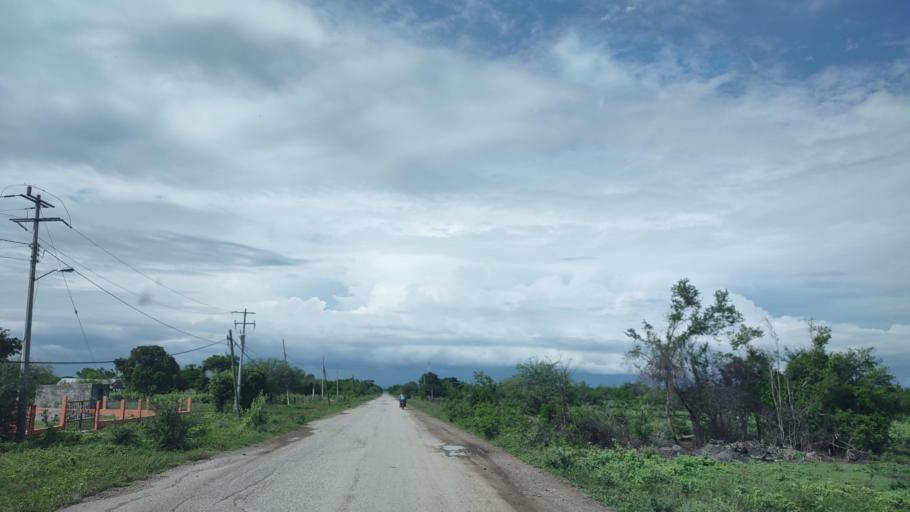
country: MX
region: Veracruz
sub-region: Panuco
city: Oviedo
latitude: 22.0069
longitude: -98.4625
